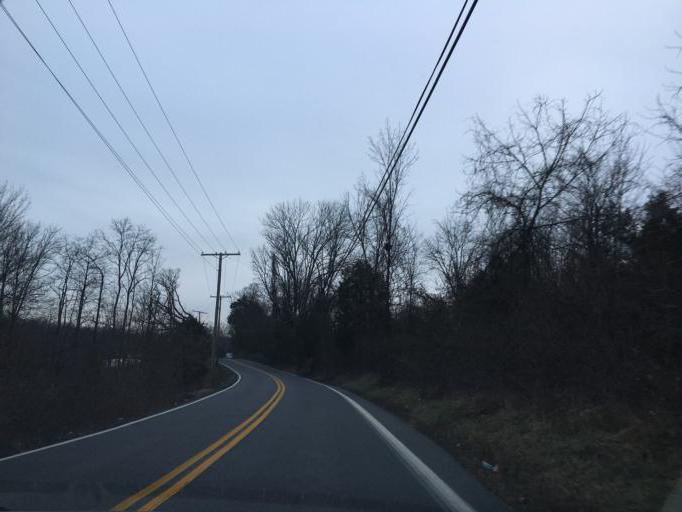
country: US
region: Maryland
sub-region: Baltimore County
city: Milford Mill
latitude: 39.3216
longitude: -76.7737
